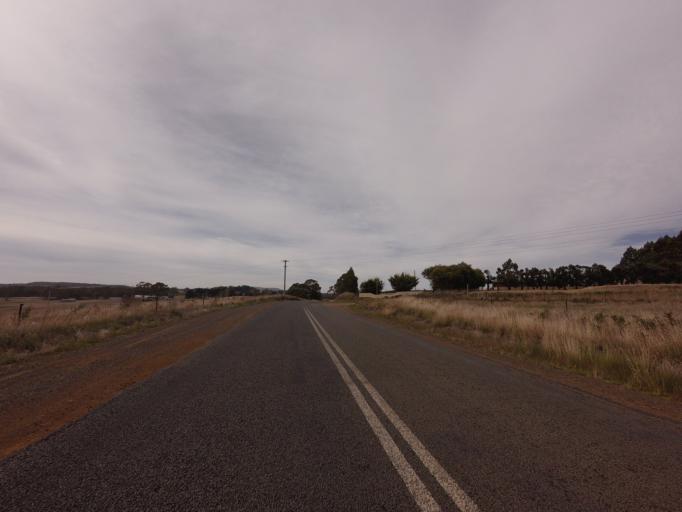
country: AU
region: Tasmania
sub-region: Brighton
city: Bridgewater
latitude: -42.3875
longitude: 147.4232
